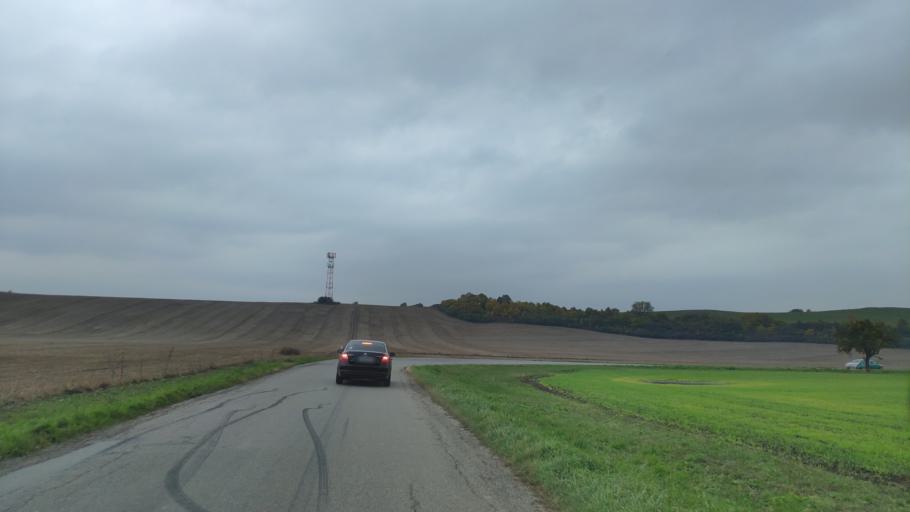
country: SK
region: Kosicky
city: Kosice
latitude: 48.6390
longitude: 21.3739
